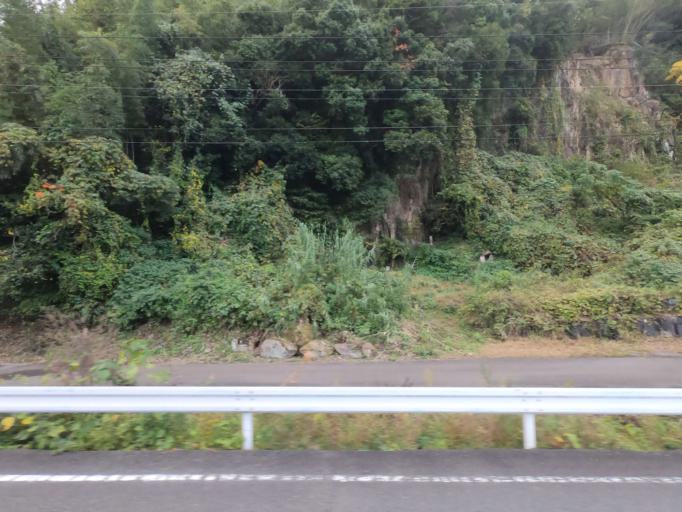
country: JP
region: Kumamoto
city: Minamata
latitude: 32.2654
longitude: 130.5068
